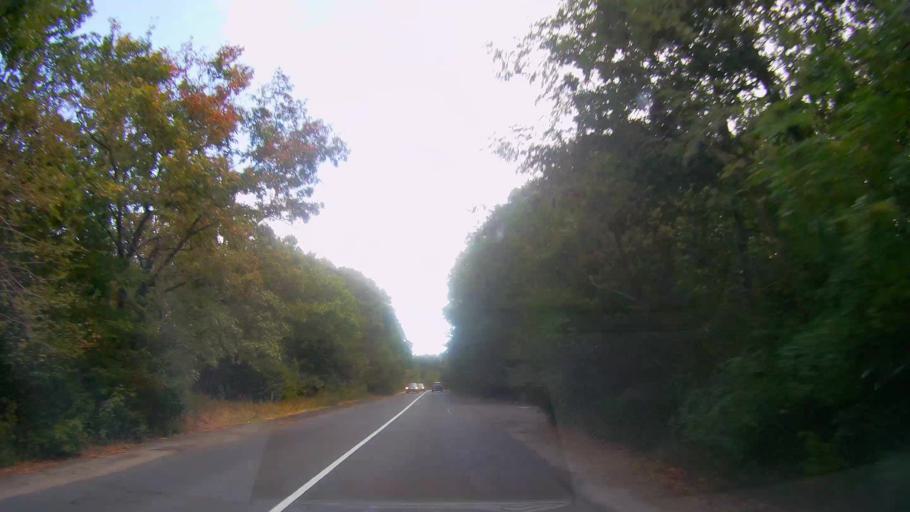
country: BG
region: Burgas
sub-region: Obshtina Primorsko
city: Primorsko
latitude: 42.2924
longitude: 27.7323
